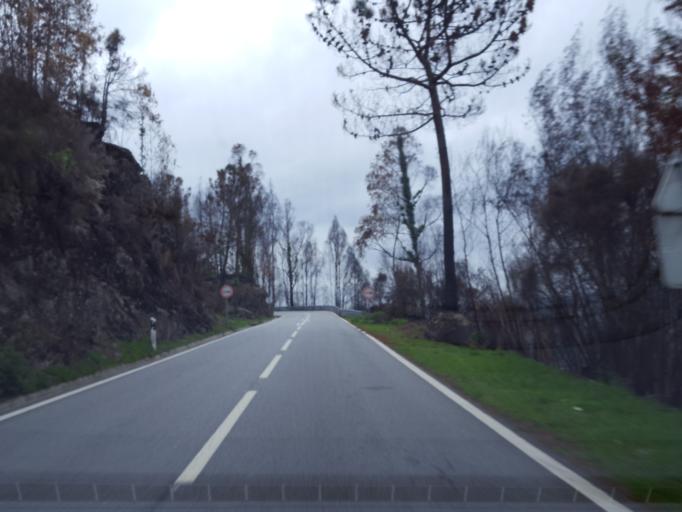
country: PT
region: Porto
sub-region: Marco de Canaveses
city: Marco de Canavezes
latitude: 41.1471
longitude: -8.1323
